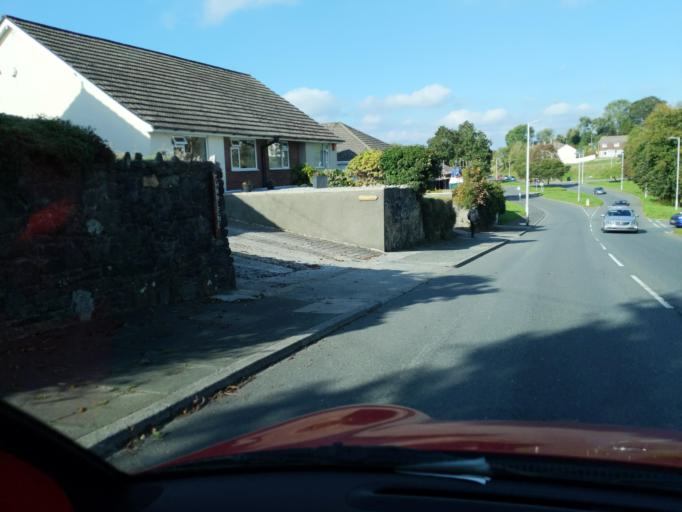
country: GB
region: England
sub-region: Plymouth
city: Plymouth
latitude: 50.4226
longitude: -4.1427
